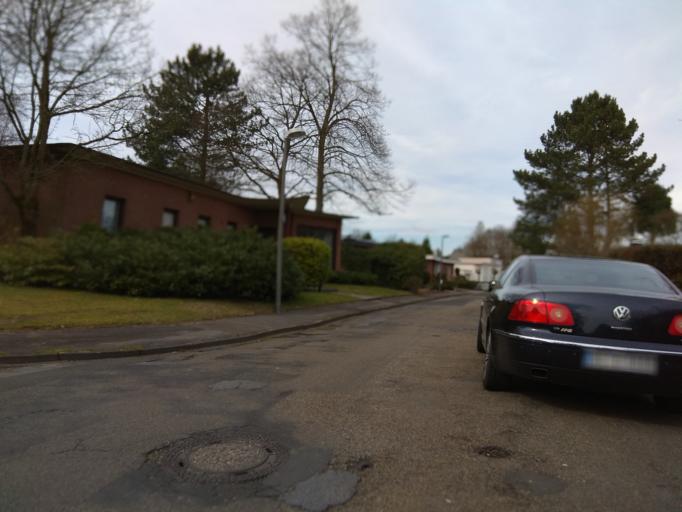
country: DE
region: North Rhine-Westphalia
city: Marl
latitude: 51.6577
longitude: 7.1240
